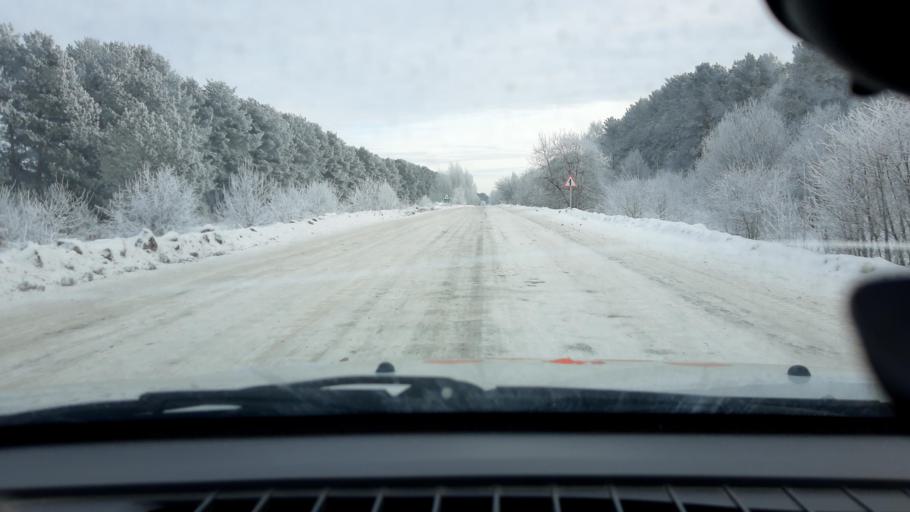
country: RU
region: Nizjnij Novgorod
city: Bogorodsk
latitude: 56.0664
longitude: 43.5920
